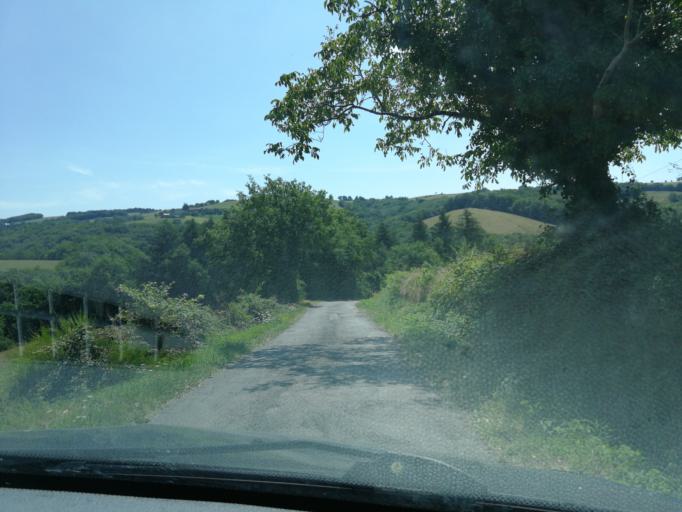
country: FR
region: Auvergne
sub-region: Departement du Cantal
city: Maurs
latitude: 44.6881
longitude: 2.3290
